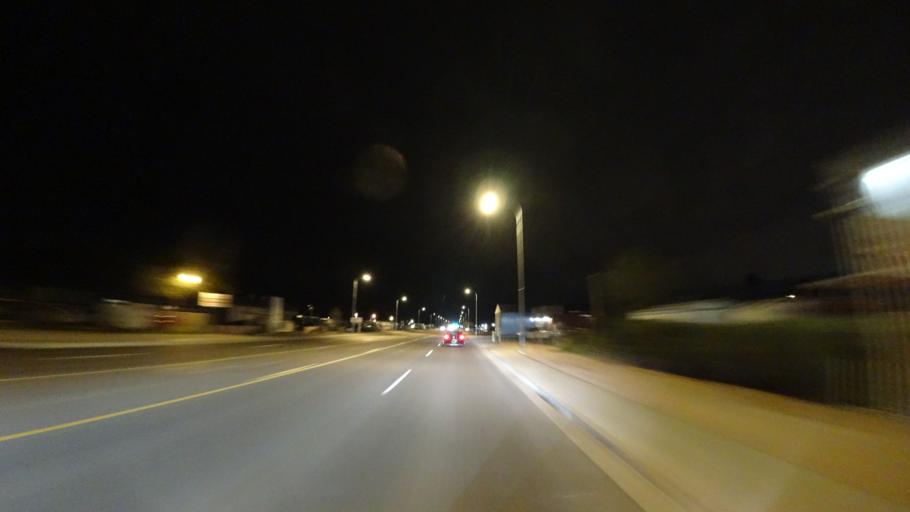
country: US
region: Arizona
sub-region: Pinal County
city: Apache Junction
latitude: 33.4133
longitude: -111.5635
